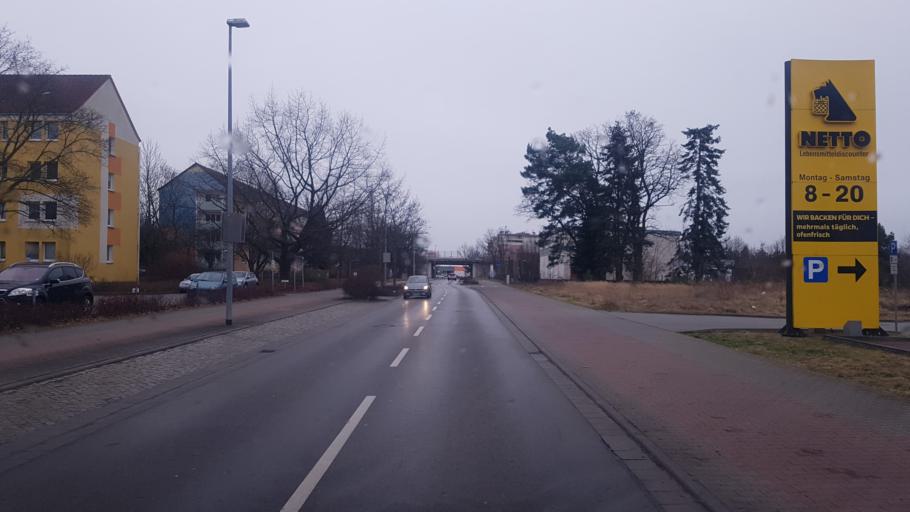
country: DE
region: Brandenburg
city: Schwarzheide
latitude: 51.4735
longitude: 13.8647
